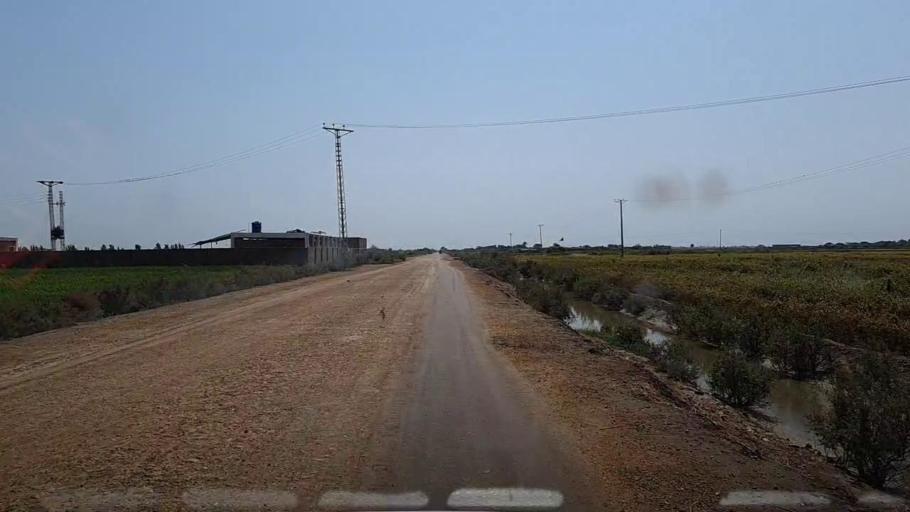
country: PK
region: Sindh
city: Mirpur Batoro
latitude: 24.6357
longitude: 68.4522
